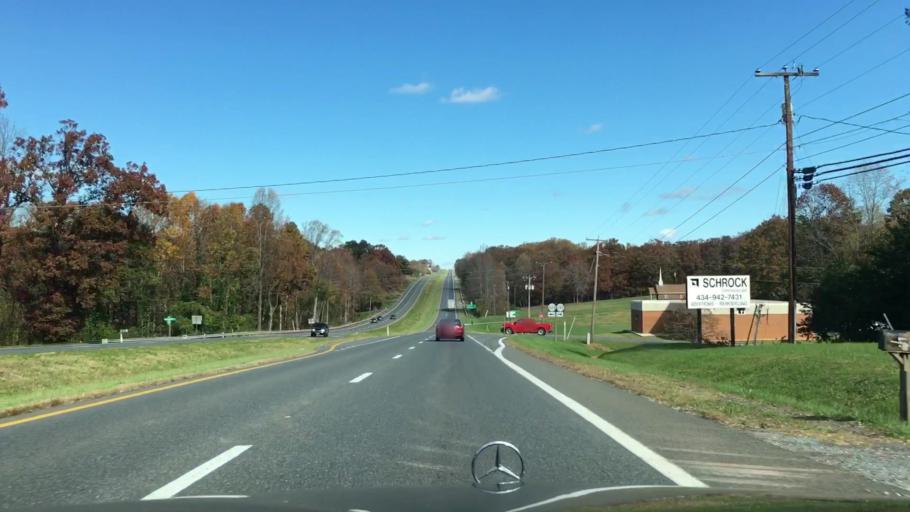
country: US
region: Virginia
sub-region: Campbell County
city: Rustburg
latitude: 37.2597
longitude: -79.1821
